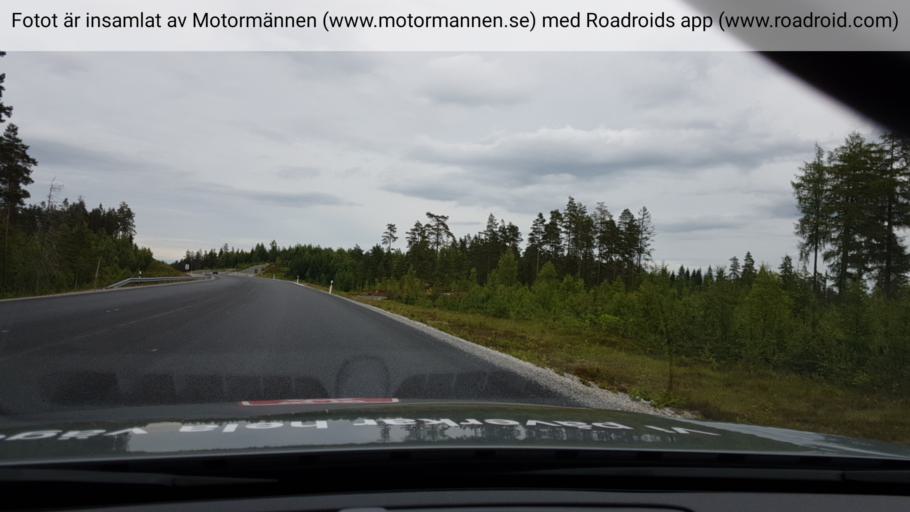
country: SE
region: Vaestmanland
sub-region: Skinnskattebergs Kommun
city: Skinnskatteberg
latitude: 59.8466
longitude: 15.5814
